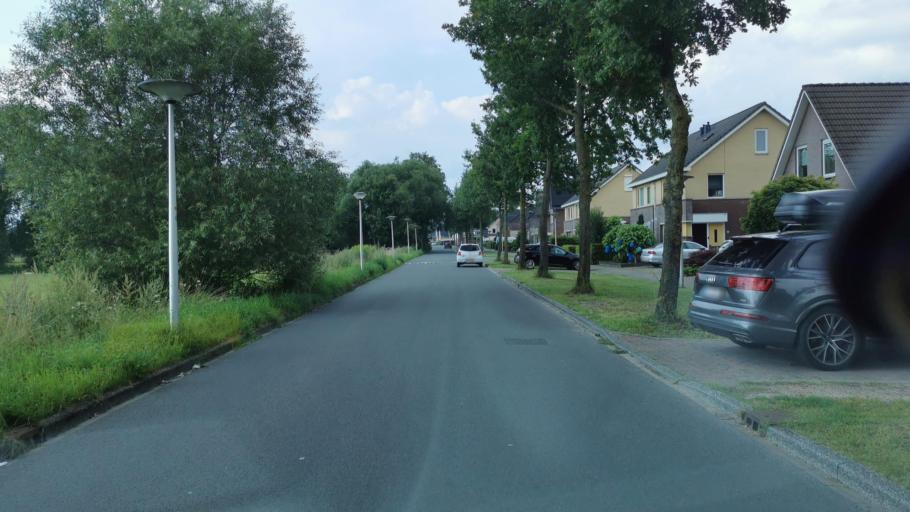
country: DE
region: North Rhine-Westphalia
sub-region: Regierungsbezirk Munster
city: Gronau
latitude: 52.2045
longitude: 6.9641
